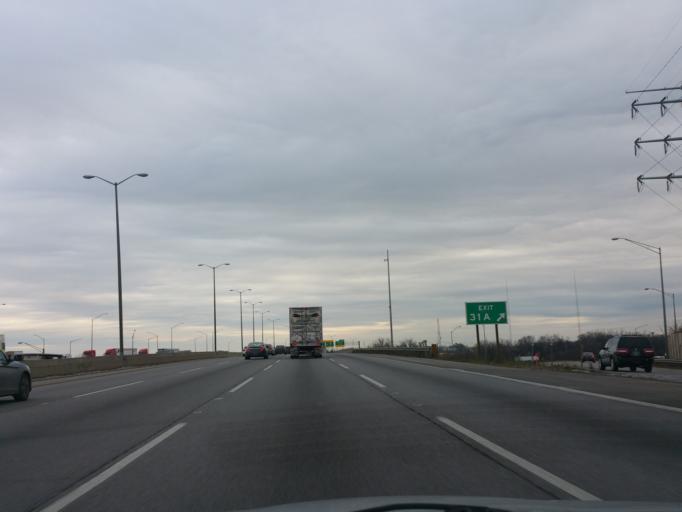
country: US
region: Illinois
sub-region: Cook County
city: Hillside
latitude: 41.8710
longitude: -87.9176
